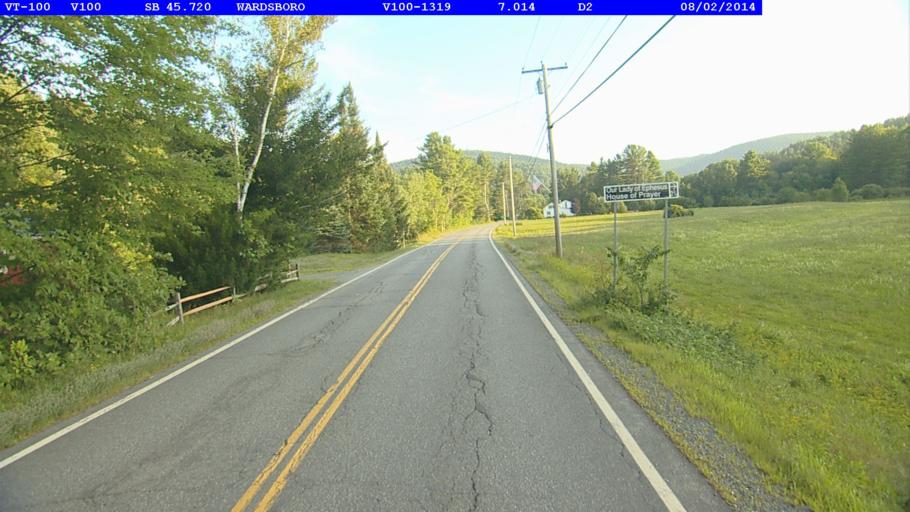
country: US
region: Vermont
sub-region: Windham County
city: Dover
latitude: 43.0465
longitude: -72.7863
